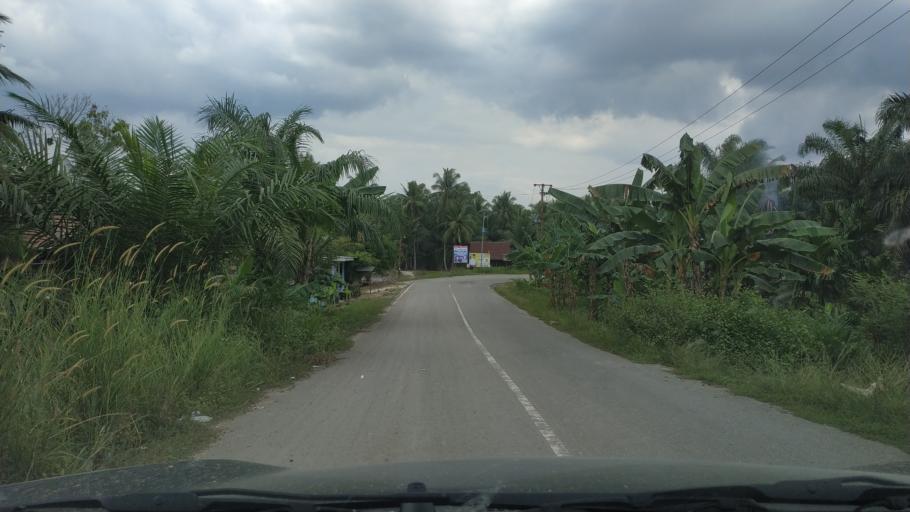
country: ID
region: Riau
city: Sungaisalak
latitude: -0.5632
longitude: 102.9652
